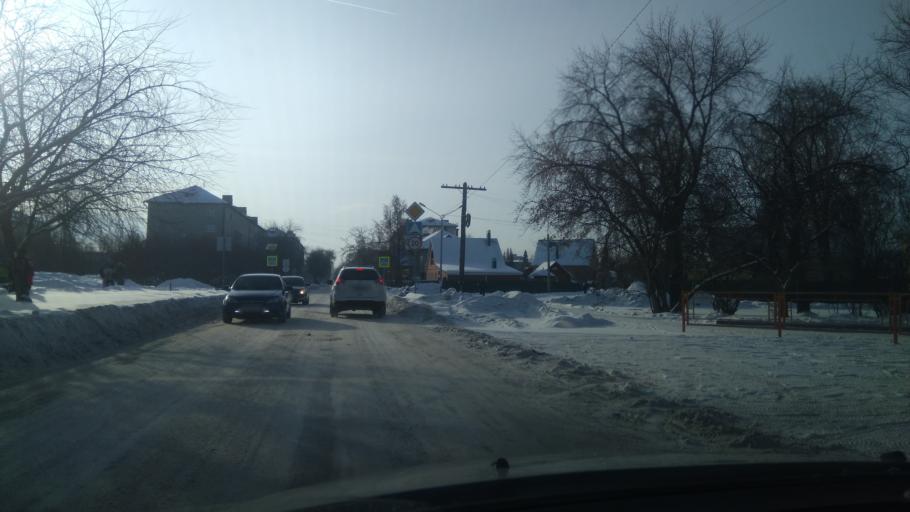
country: RU
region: Sverdlovsk
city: Sukhoy Log
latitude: 56.9054
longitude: 62.0327
